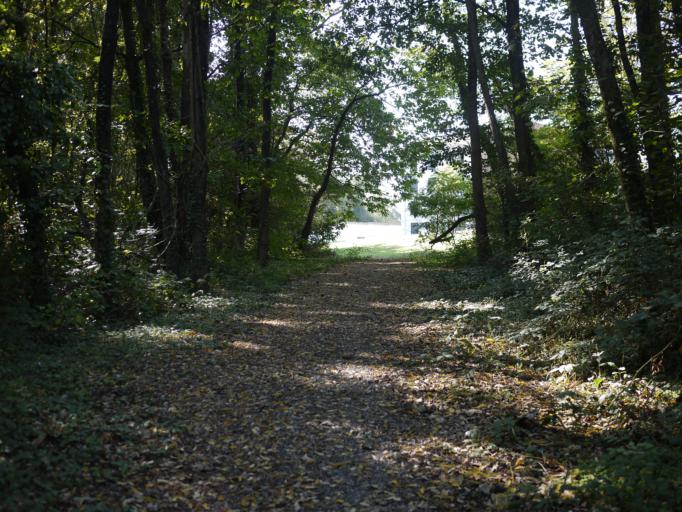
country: FR
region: Aquitaine
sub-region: Departement des Landes
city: Saint-Paul-les-Dax
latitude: 43.7239
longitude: -1.0772
